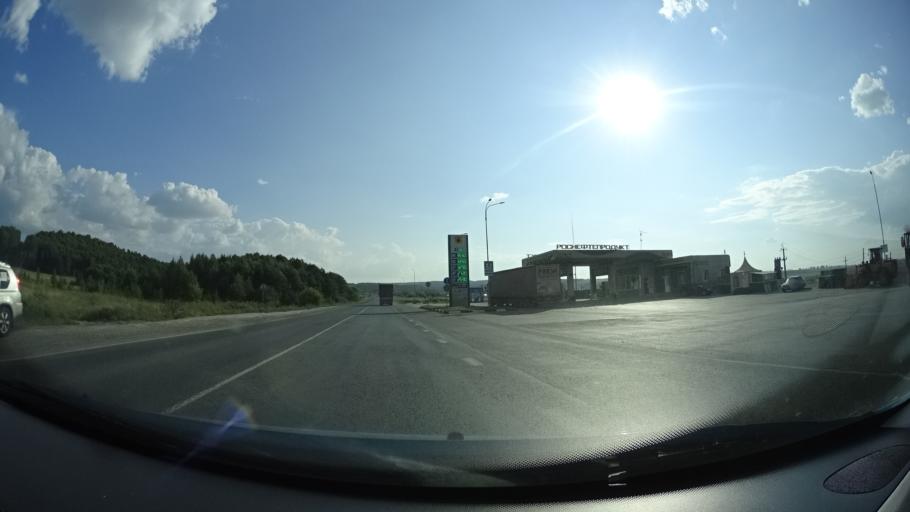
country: RU
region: Tatarstan
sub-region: Bavlinskiy Rayon
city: Bavly
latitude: 54.4667
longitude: 53.2969
